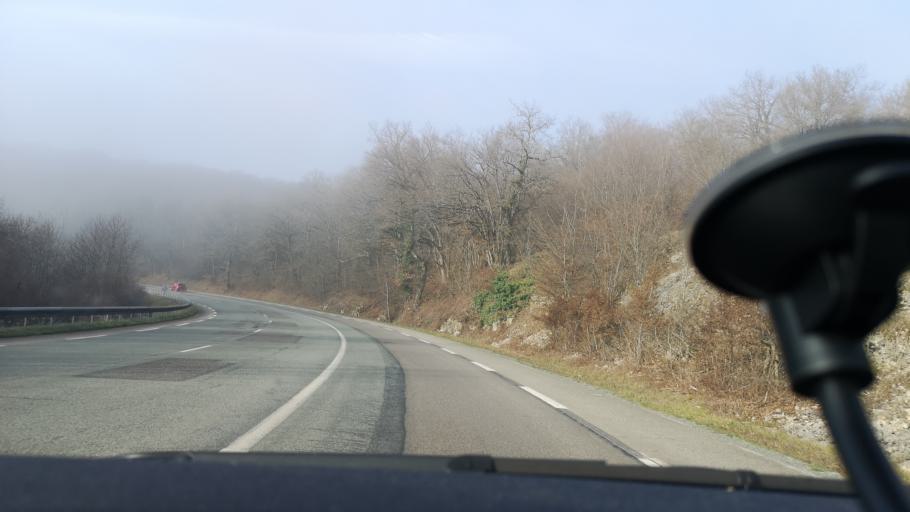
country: FR
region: Franche-Comte
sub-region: Departement du Doubs
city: Clerval
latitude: 47.4308
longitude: 6.5704
